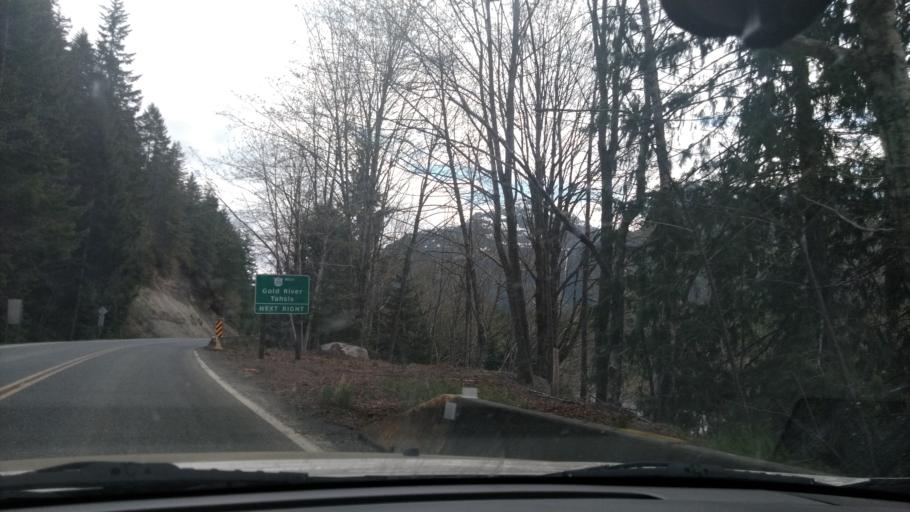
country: CA
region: British Columbia
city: Campbell River
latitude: 49.8403
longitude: -125.6261
